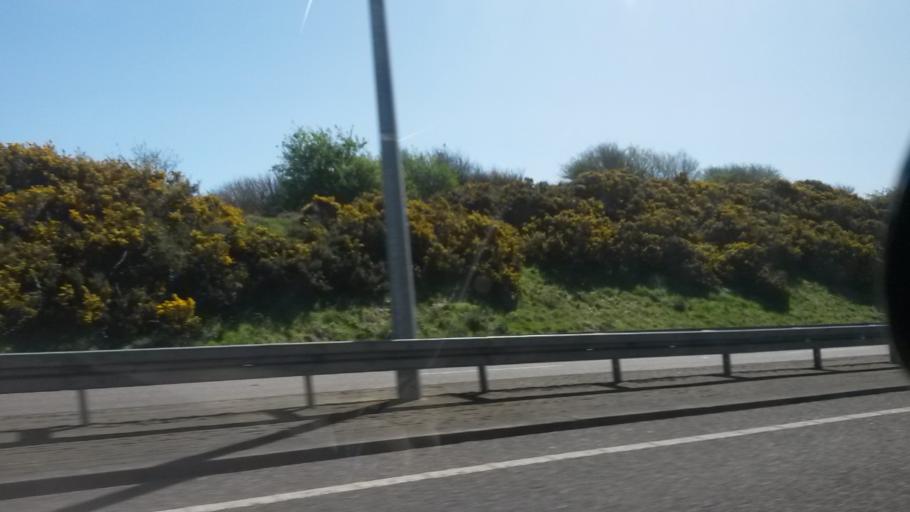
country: IE
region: Munster
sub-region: County Cork
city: Tower
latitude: 51.8819
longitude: -8.5714
